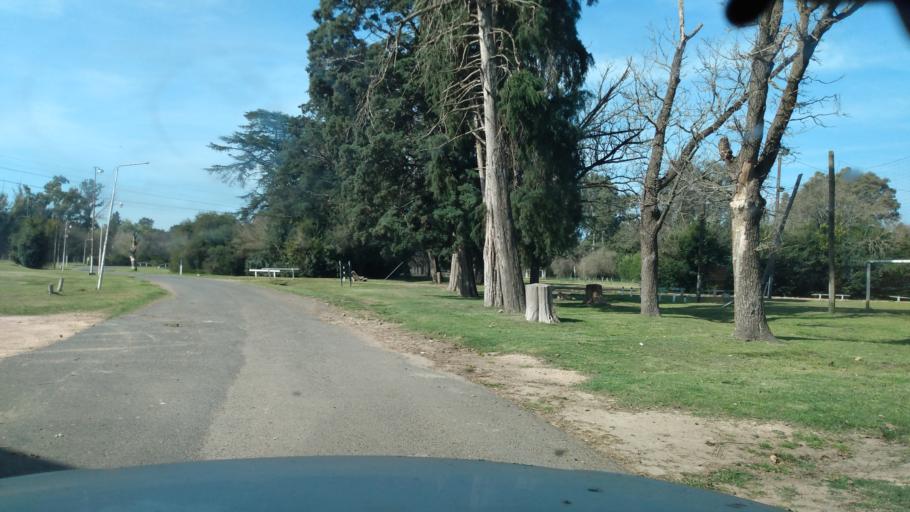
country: AR
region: Buenos Aires
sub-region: Partido de Lujan
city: Lujan
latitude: -34.5936
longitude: -59.1853
